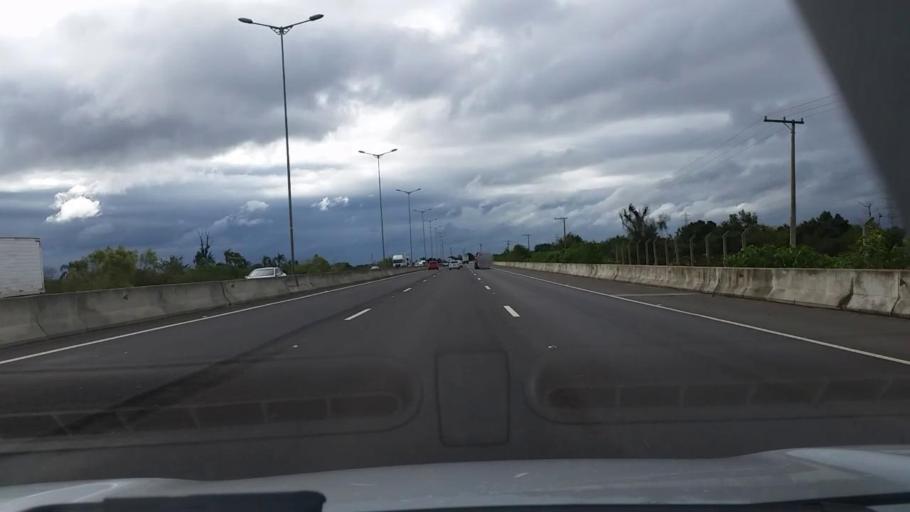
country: BR
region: Rio Grande do Sul
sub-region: Canoas
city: Canoas
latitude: -29.9464
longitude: -51.2041
